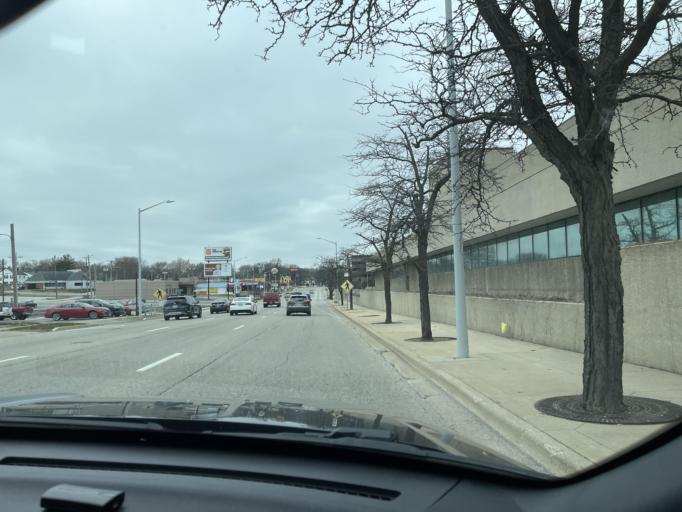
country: US
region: Illinois
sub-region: Sangamon County
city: Springfield
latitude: 39.8030
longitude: -89.6577
